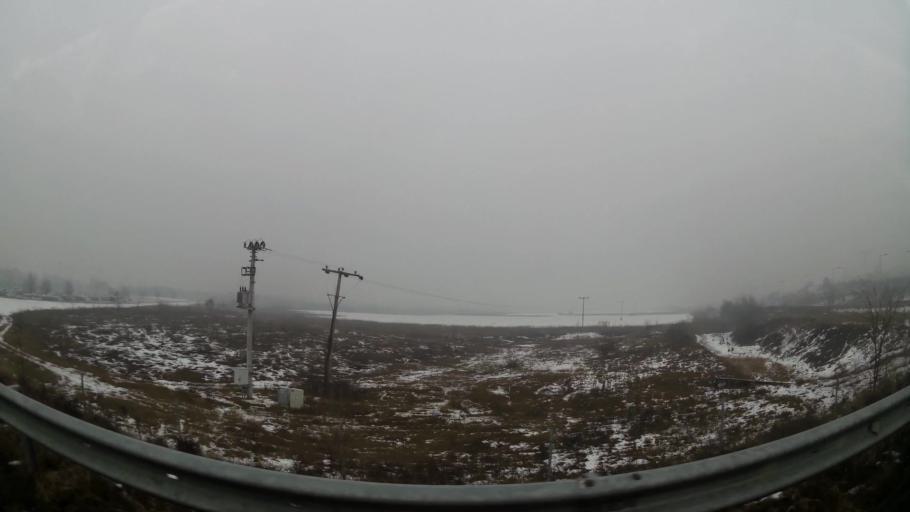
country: MK
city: Miladinovci
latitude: 41.9594
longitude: 21.6313
